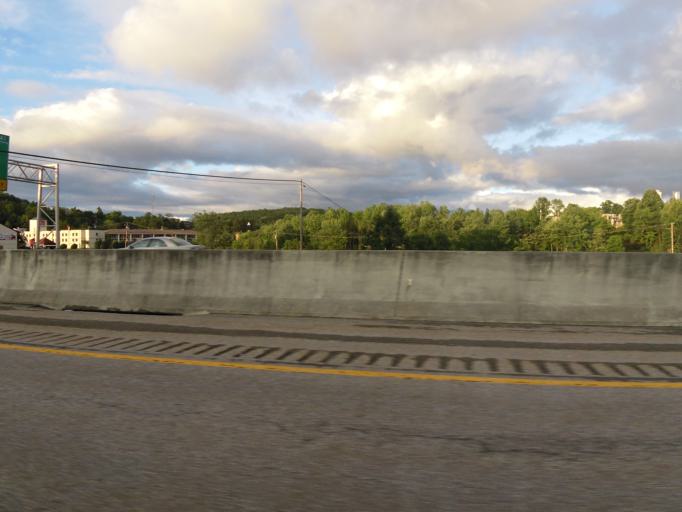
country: US
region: Kentucky
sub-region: Laurel County
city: London
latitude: 37.1419
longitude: -84.1104
